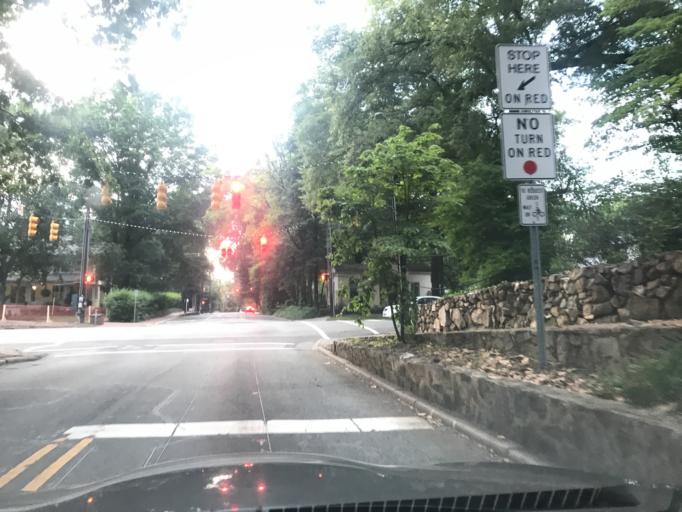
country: US
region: North Carolina
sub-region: Orange County
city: Chapel Hill
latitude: 35.9153
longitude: -79.0490
